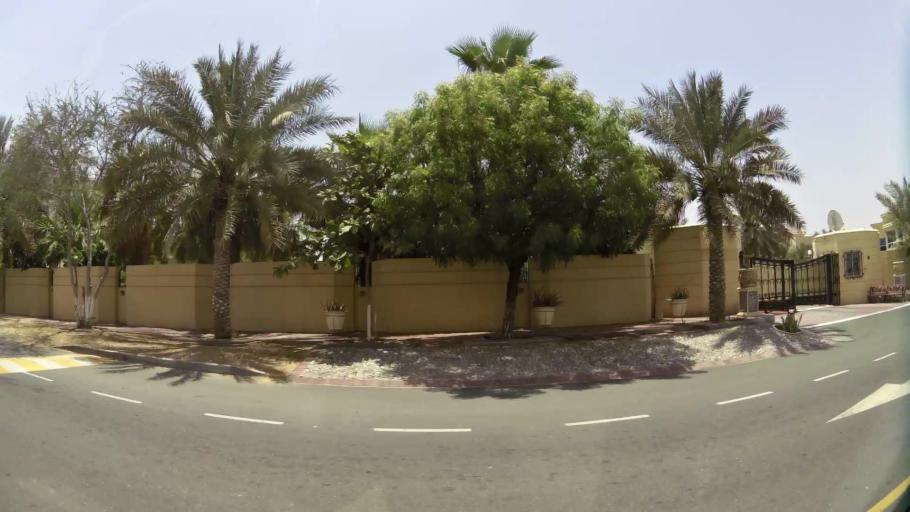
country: AE
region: Ash Shariqah
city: Sharjah
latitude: 25.2351
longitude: 55.4838
